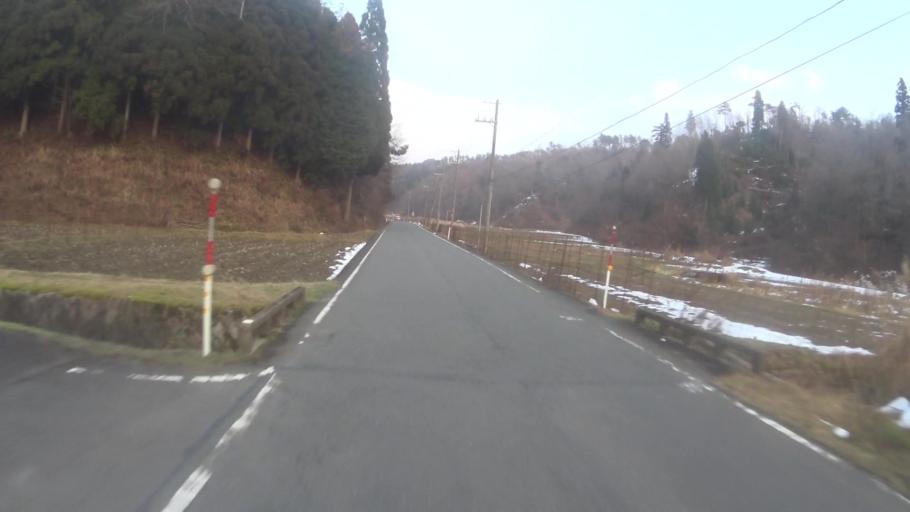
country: JP
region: Kyoto
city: Maizuru
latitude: 35.4355
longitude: 135.4800
